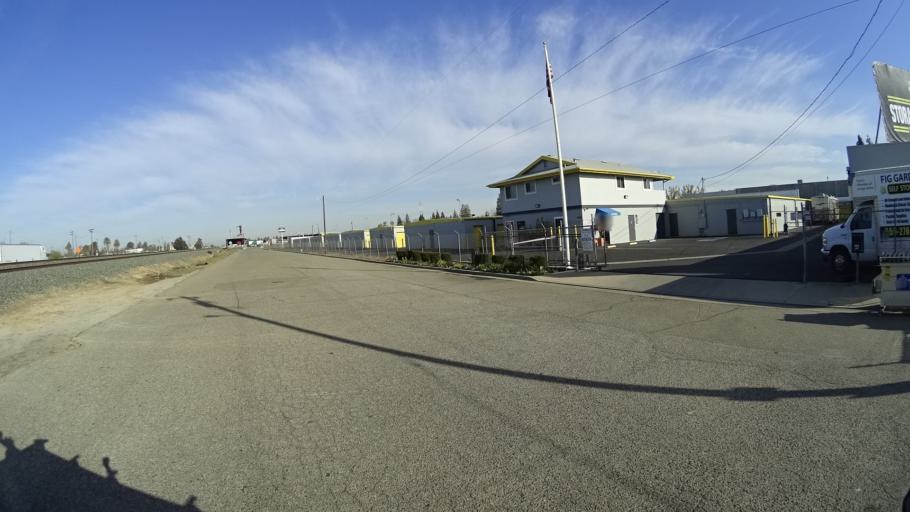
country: US
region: California
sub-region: Fresno County
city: West Park
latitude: 36.8096
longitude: -119.8785
